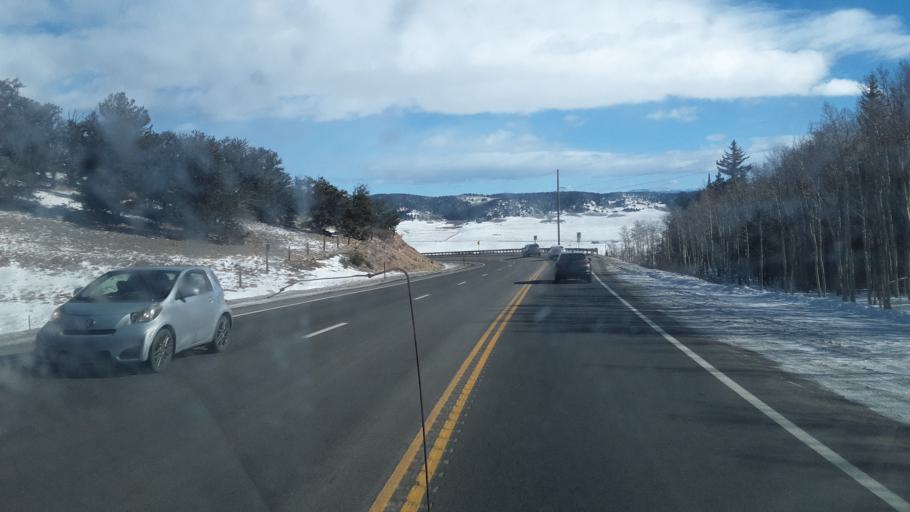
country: US
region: Colorado
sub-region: Park County
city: Fairplay
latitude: 39.2625
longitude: -105.9601
